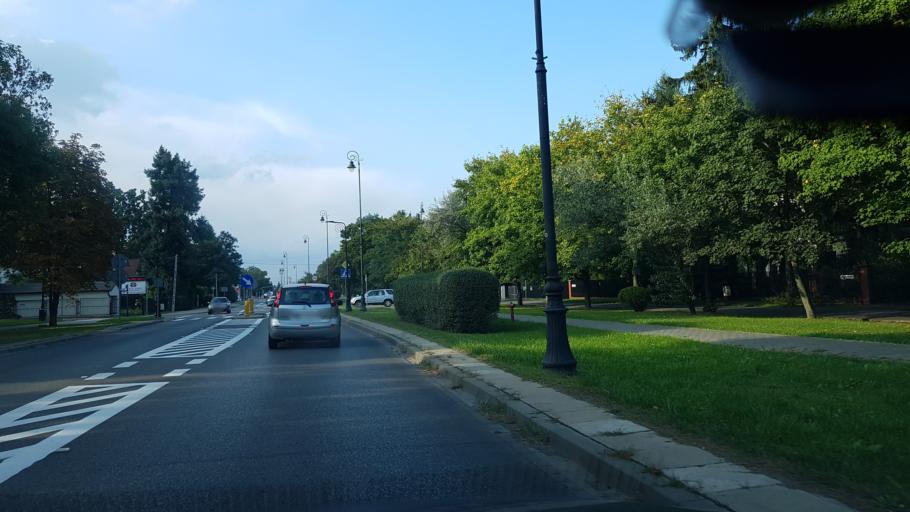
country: PL
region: Masovian Voivodeship
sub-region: Powiat piaseczynski
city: Konstancin-Jeziorna
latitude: 52.0998
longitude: 21.1157
